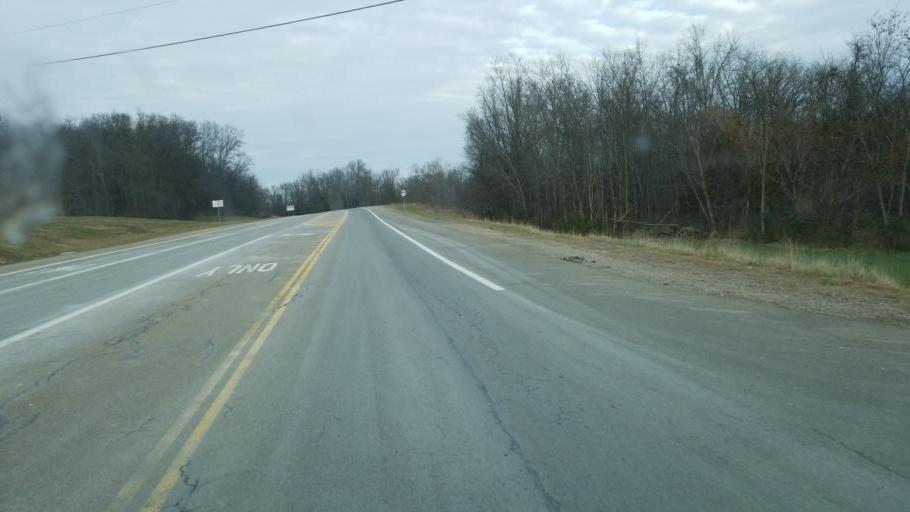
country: US
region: Ohio
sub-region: Muskingum County
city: Dresden
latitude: 40.1096
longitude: -82.0147
